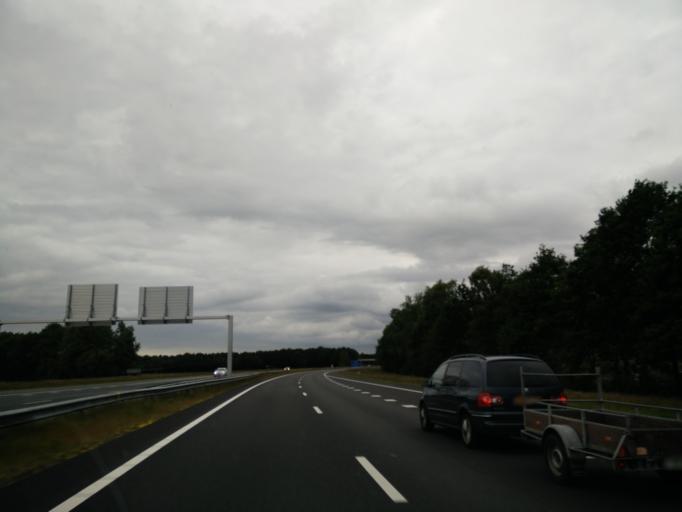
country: NL
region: Drenthe
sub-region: Gemeente Assen
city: Assen
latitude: 52.9790
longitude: 6.5305
